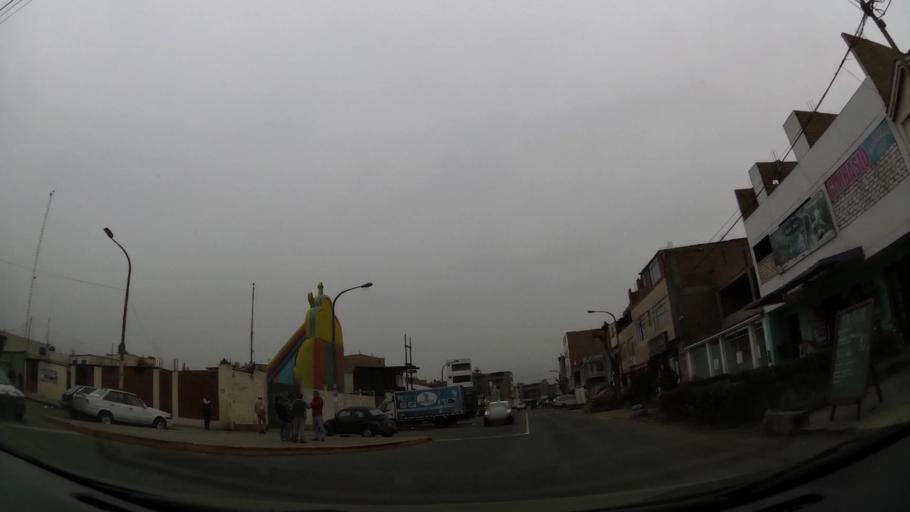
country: PE
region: Lima
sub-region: Lima
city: Independencia
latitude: -11.9349
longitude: -77.0785
